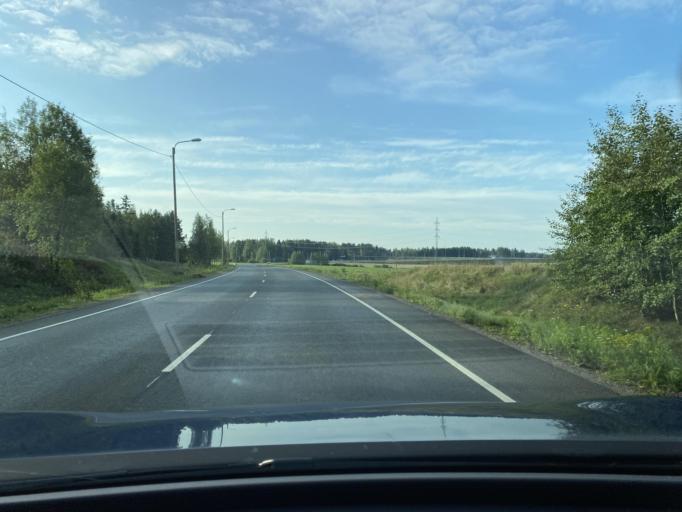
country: FI
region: Kymenlaakso
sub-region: Kouvola
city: Kouvola
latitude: 60.8802
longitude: 26.6011
